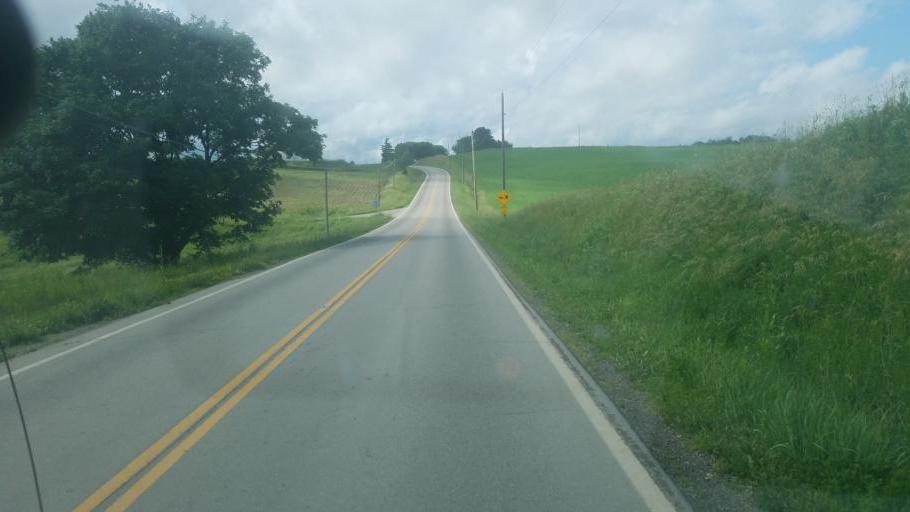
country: US
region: Ohio
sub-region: Carroll County
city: Carrollton
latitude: 40.4680
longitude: -81.0025
